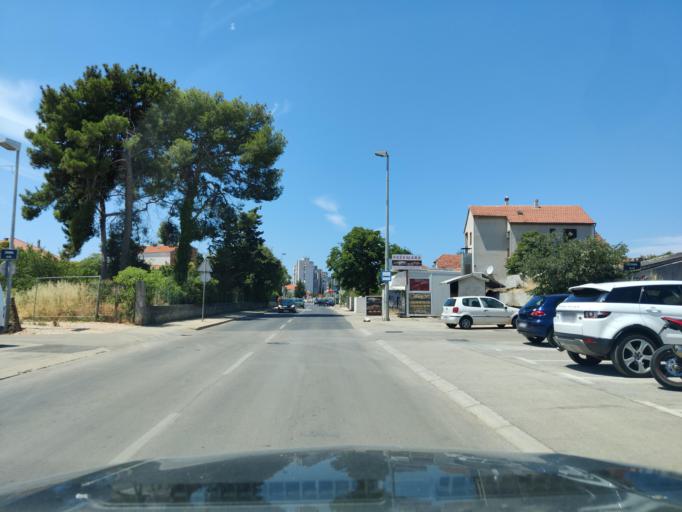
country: HR
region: Zadarska
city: Zadar
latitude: 44.1059
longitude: 15.2532
